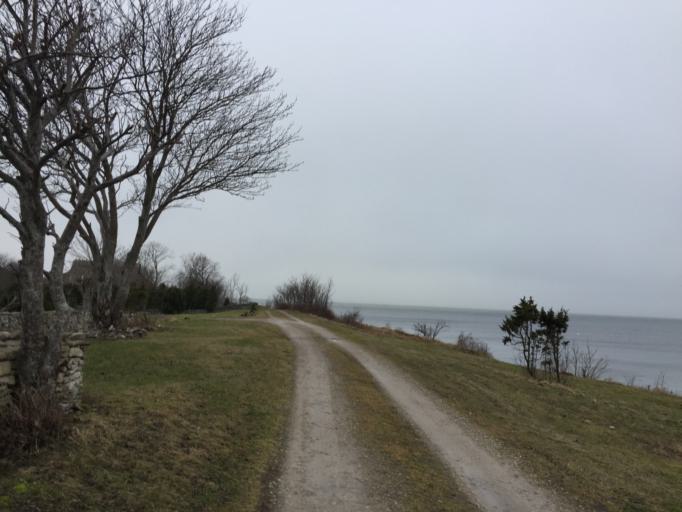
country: EE
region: Saare
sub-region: Kuressaare linn
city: Kuressaare
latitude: 58.5461
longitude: 22.2151
